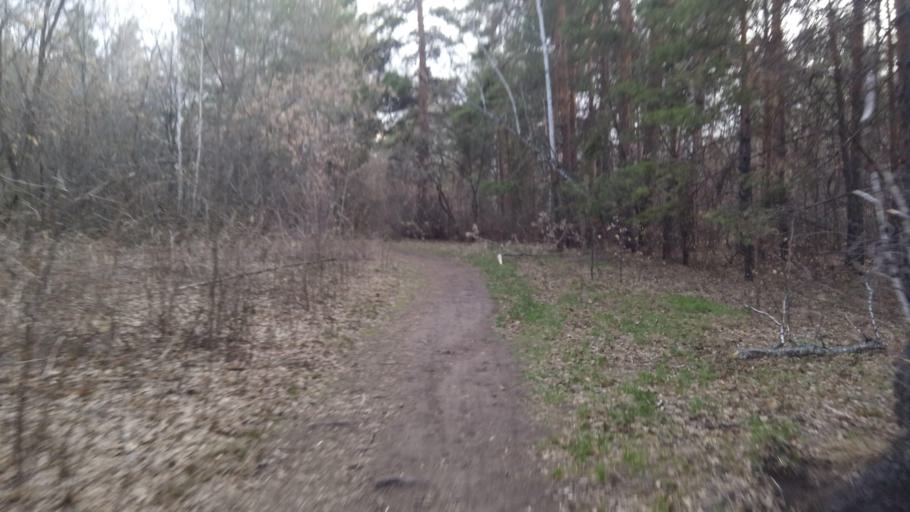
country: RU
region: Chelyabinsk
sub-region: Gorod Chelyabinsk
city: Chelyabinsk
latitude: 55.1452
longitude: 61.3404
